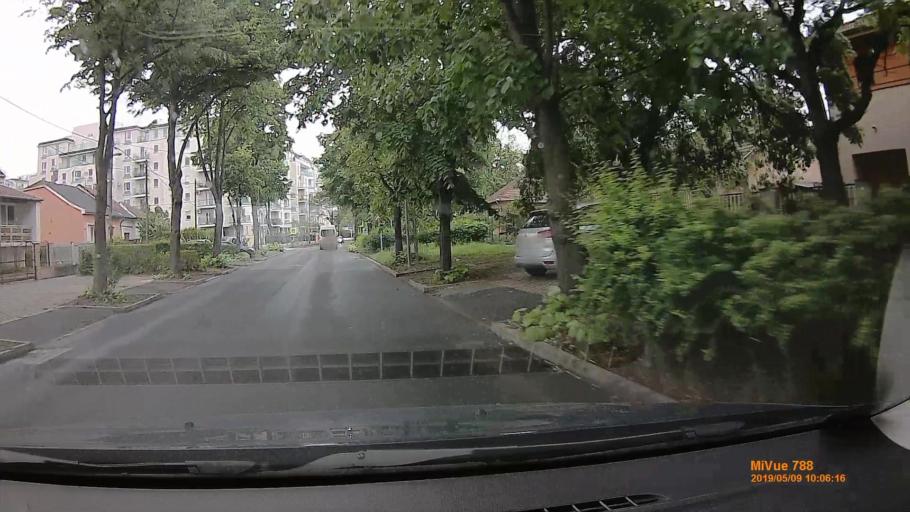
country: HU
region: Budapest
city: Budapest XIV. keruelet
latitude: 47.5338
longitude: 19.1072
